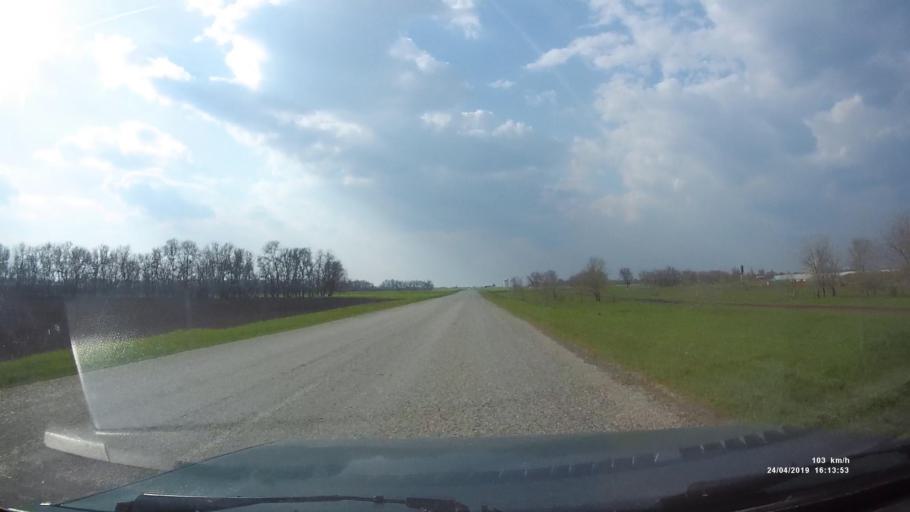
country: RU
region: Rostov
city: Sovetskoye
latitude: 46.7466
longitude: 42.2112
